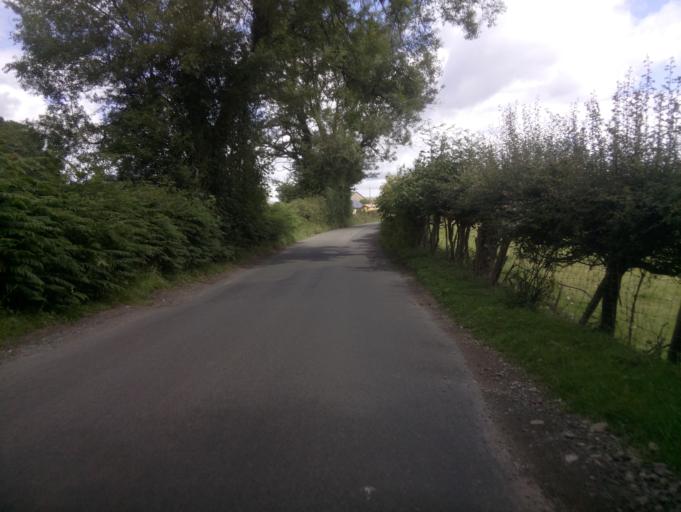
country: GB
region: England
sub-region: Gloucestershire
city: Bream
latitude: 51.7429
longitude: -2.5579
